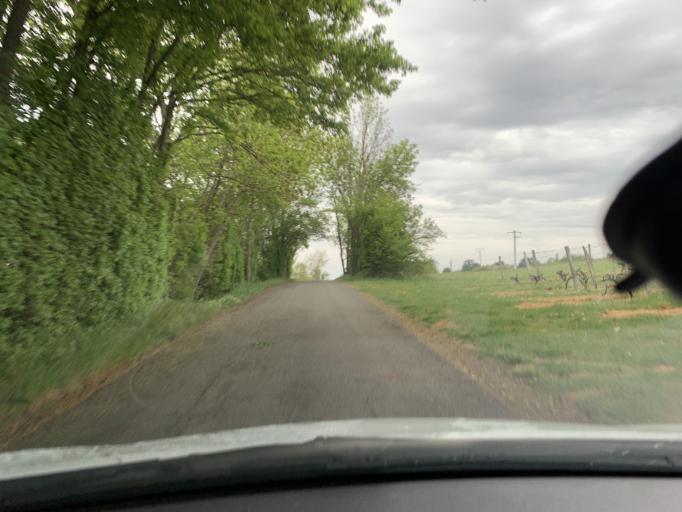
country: FR
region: Rhone-Alpes
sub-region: Departement du Rhone
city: Charnay
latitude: 45.9127
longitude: 4.6742
